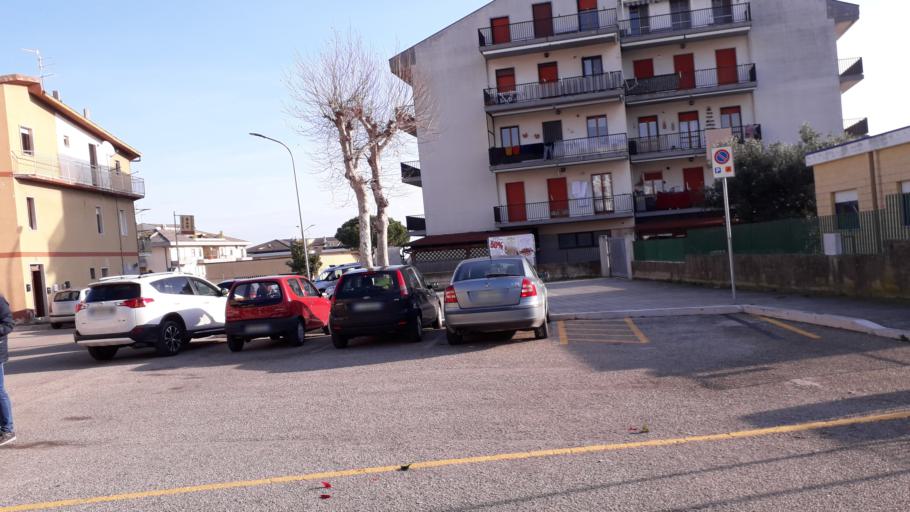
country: IT
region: Molise
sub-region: Provincia di Campobasso
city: Campomarino
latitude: 41.9541
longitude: 15.0326
